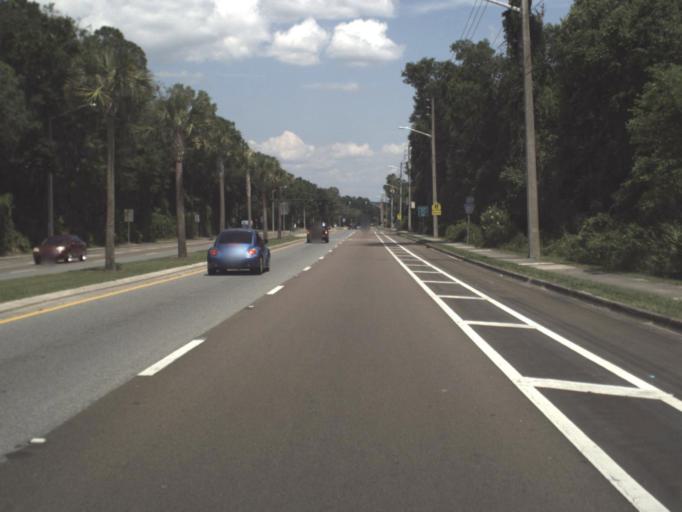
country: US
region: Florida
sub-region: Alachua County
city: Gainesville
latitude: 29.6361
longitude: -82.2745
